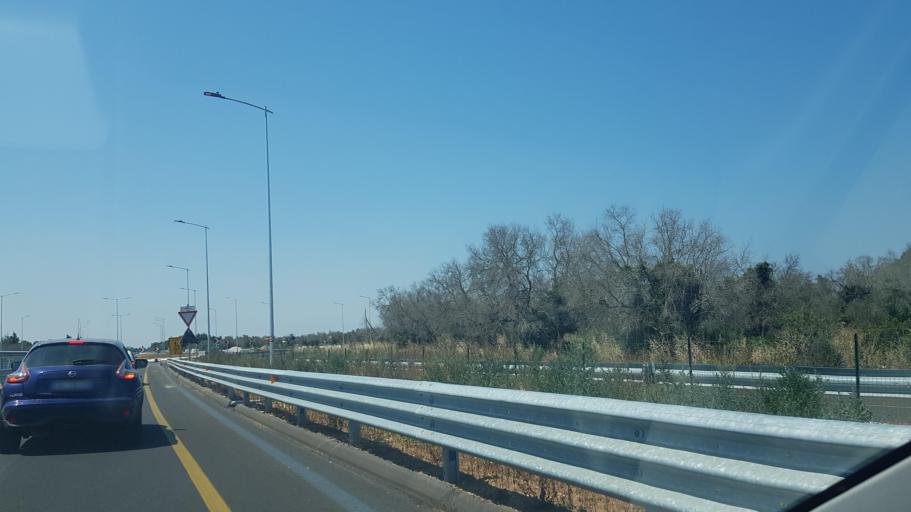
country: IT
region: Apulia
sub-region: Provincia di Lecce
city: Struda
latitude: 40.3240
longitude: 18.2614
